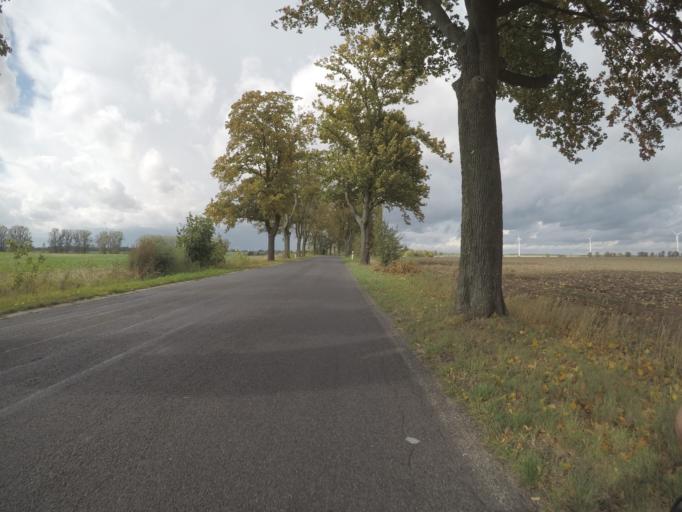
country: DE
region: Brandenburg
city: Altlandsberg
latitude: 52.5940
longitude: 13.7707
